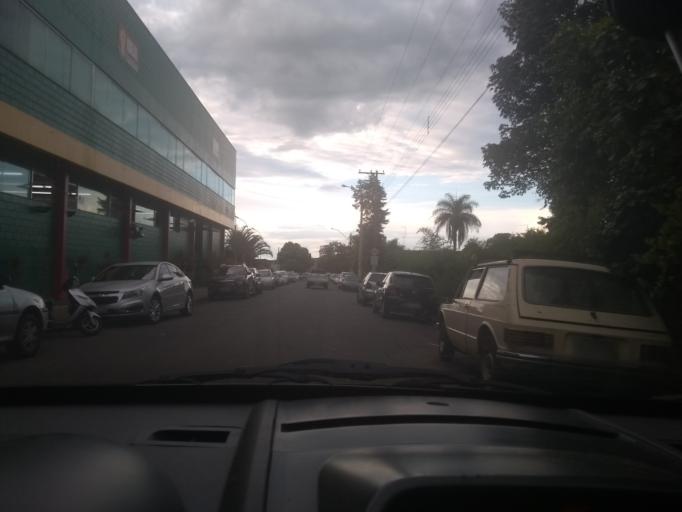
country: BR
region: Sao Paulo
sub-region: Casa Branca
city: Casa Branca
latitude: -21.7781
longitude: -47.0858
